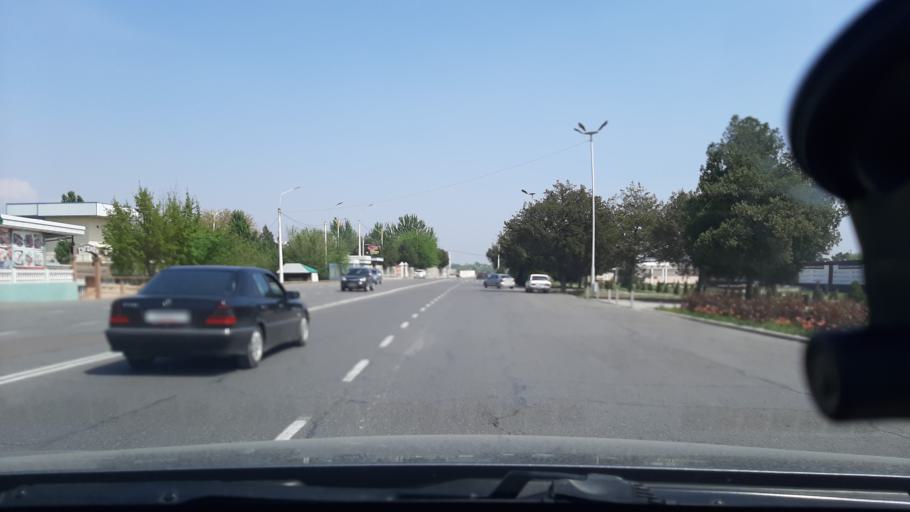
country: TJ
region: Viloyati Sughd
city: Khujand
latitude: 40.2908
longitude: 69.6248
